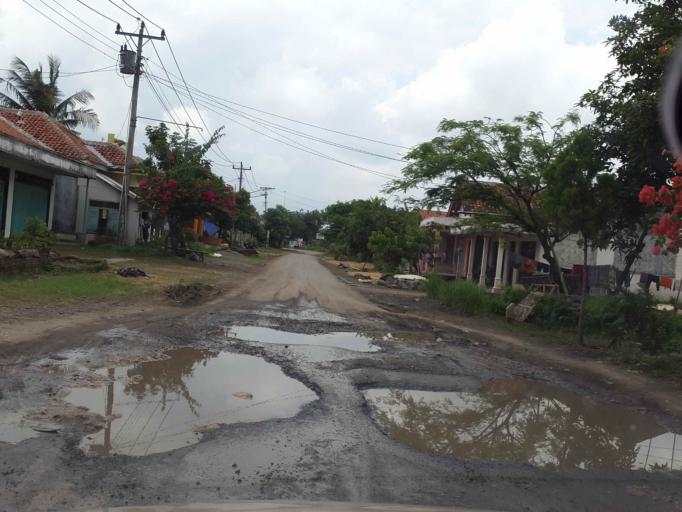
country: ID
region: Central Java
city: Ketanggungan
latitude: -6.9823
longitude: 108.9745
